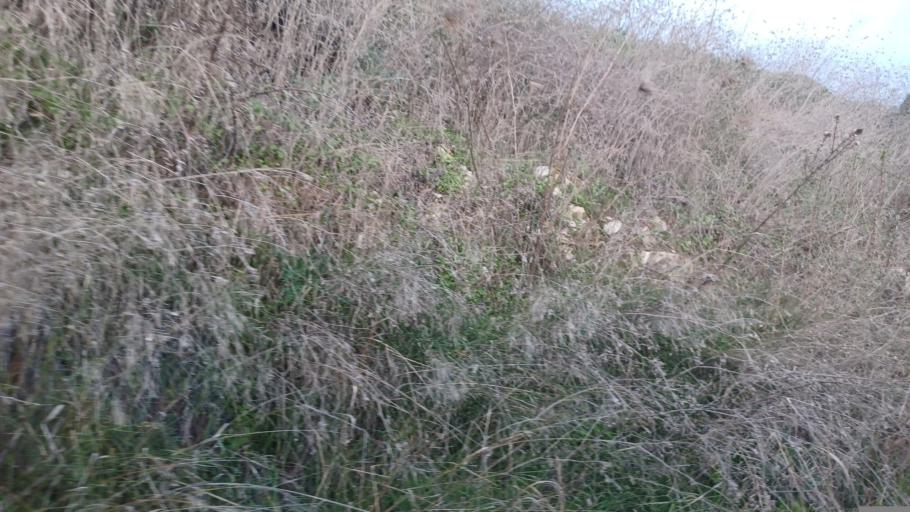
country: CY
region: Pafos
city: Mesogi
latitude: 34.8649
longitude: 32.5148
